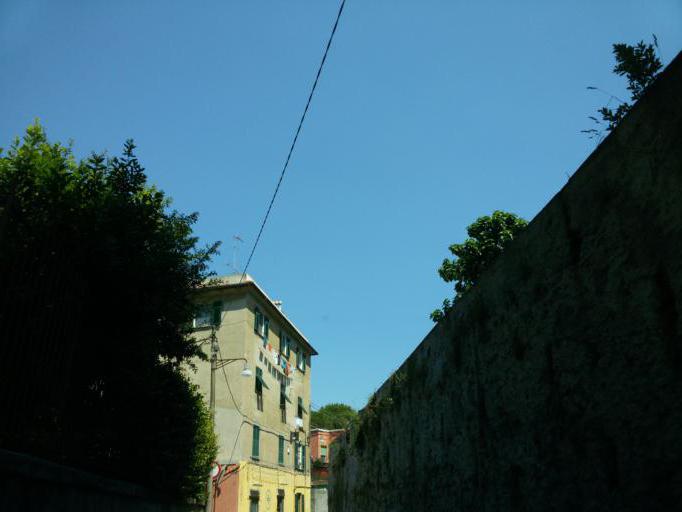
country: IT
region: Liguria
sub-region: Provincia di Genova
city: Genoa
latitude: 44.4375
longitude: 8.8750
